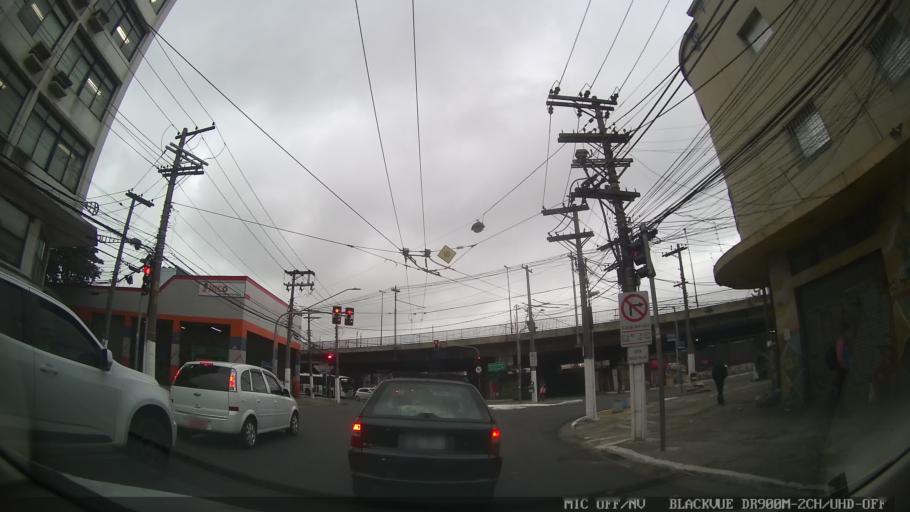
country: BR
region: Sao Paulo
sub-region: Sao Paulo
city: Sao Paulo
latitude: -23.5534
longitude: -46.5709
